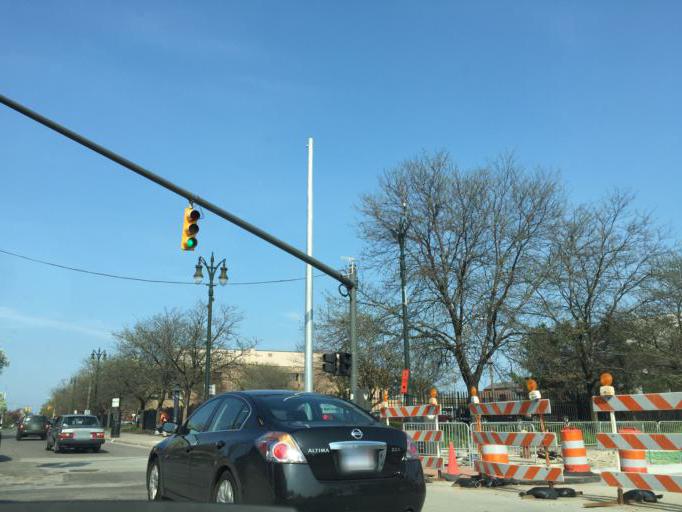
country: US
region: Michigan
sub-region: Wayne County
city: Detroit
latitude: 42.3474
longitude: -83.0580
